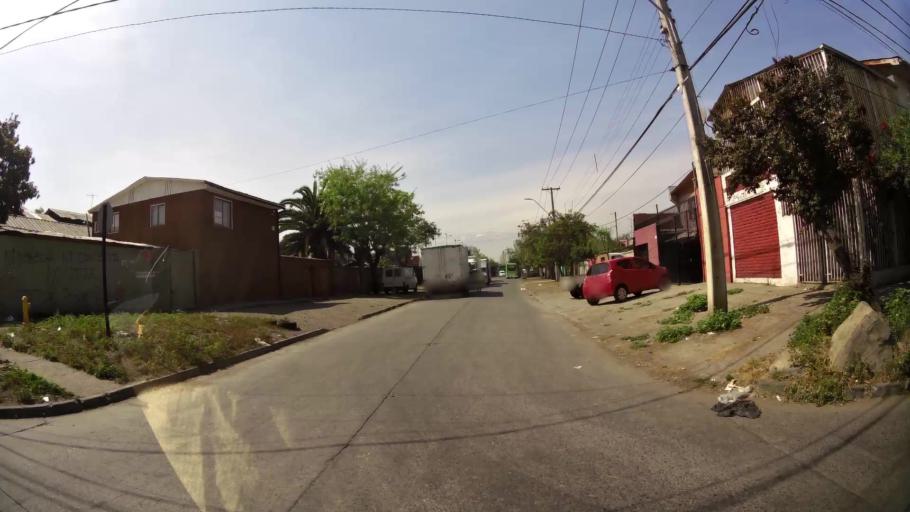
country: CL
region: Santiago Metropolitan
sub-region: Provincia de Santiago
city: Lo Prado
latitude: -33.4262
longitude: -70.7216
